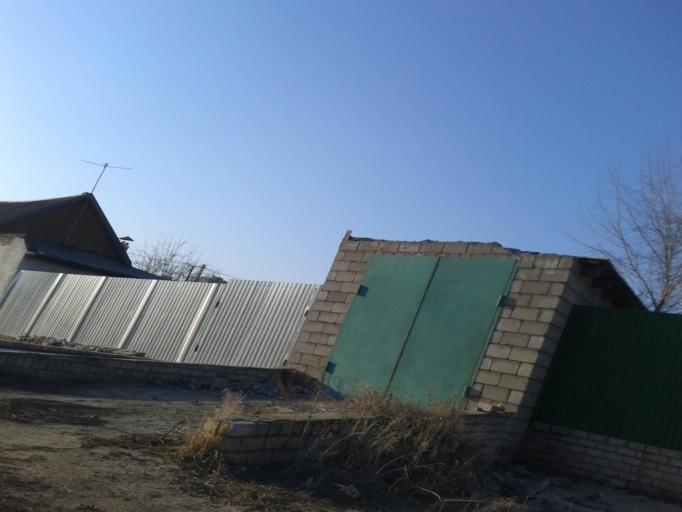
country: RU
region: Volgograd
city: Gorodishche
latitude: 48.7622
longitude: 44.4848
